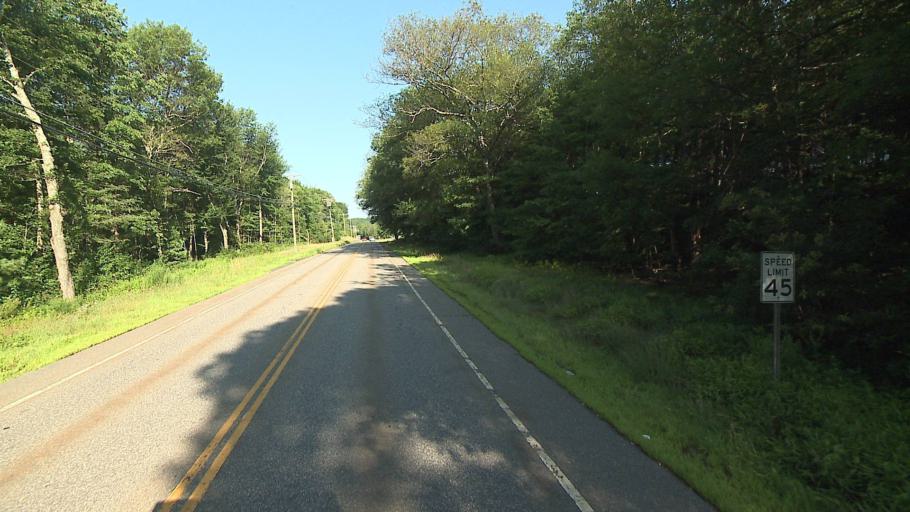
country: US
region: Connecticut
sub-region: Hartford County
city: Collinsville
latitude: 41.7774
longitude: -72.9858
